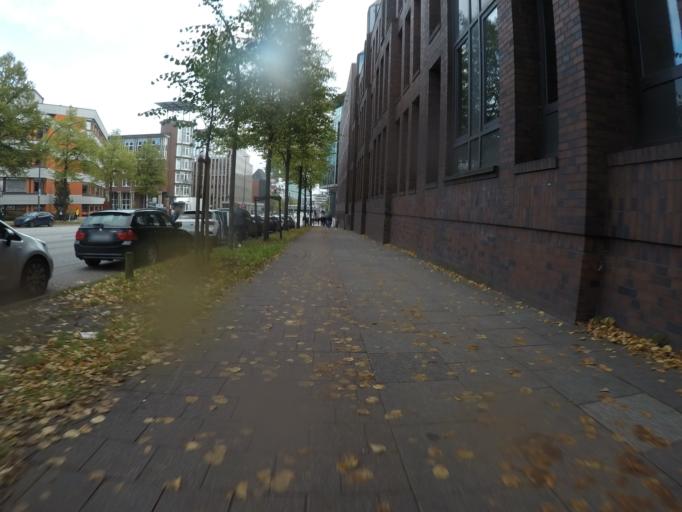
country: DE
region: Hamburg
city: Neustadt
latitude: 53.5482
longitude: 9.9821
